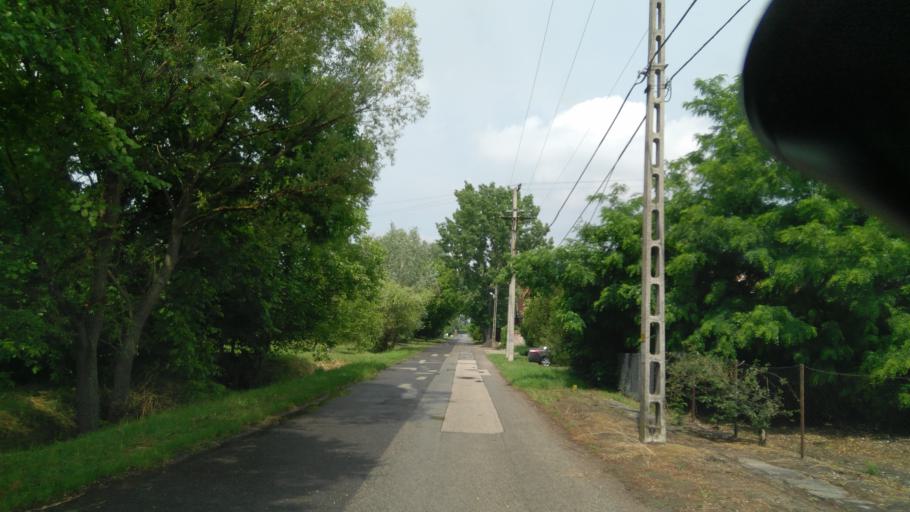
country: HU
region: Bekes
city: Bekescsaba
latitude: 46.6670
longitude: 21.1736
